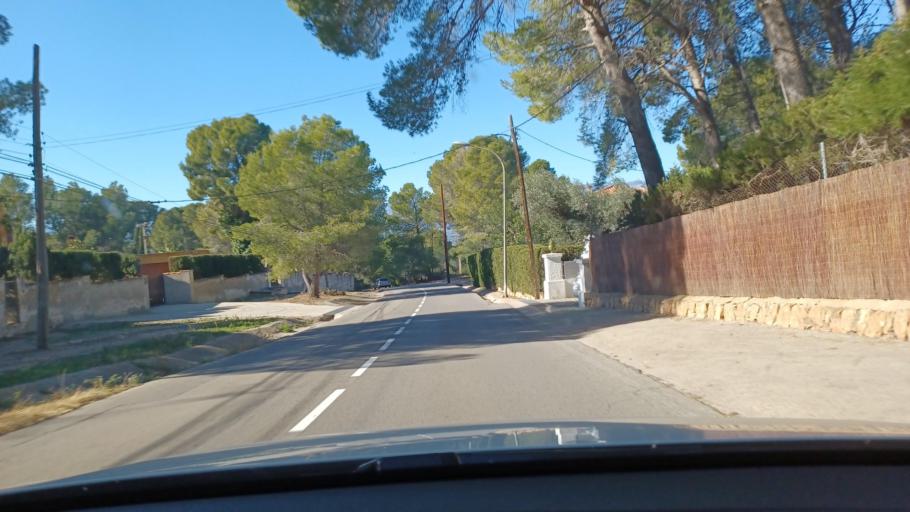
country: ES
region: Catalonia
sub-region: Provincia de Tarragona
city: Tortosa
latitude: 40.8133
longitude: 0.5419
